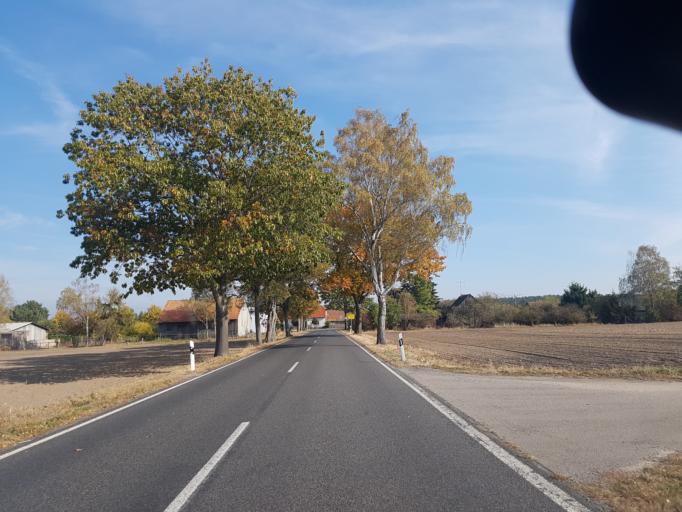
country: DE
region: Brandenburg
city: Lebusa
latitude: 51.8295
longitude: 13.3879
